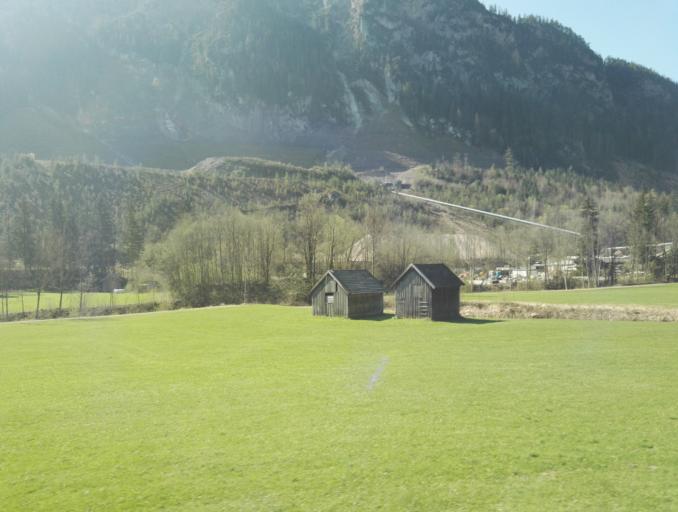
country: AT
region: Salzburg
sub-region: Politischer Bezirk Sankt Johann im Pongau
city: Forstau
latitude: 47.3954
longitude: 13.5176
